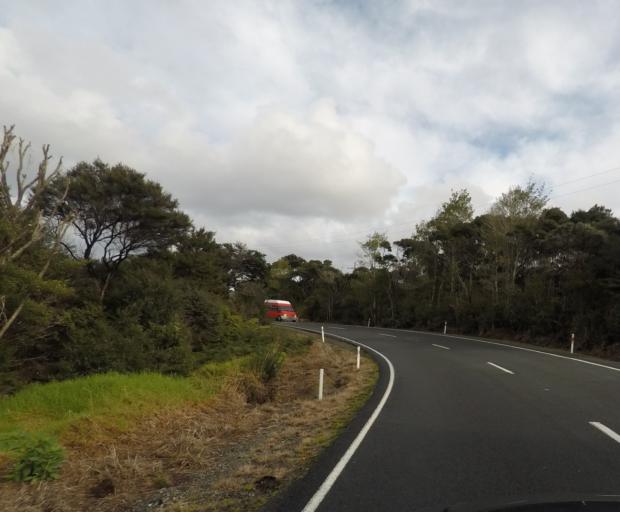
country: NZ
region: Northland
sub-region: Whangarei
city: Ruakaka
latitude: -36.0533
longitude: 174.5493
